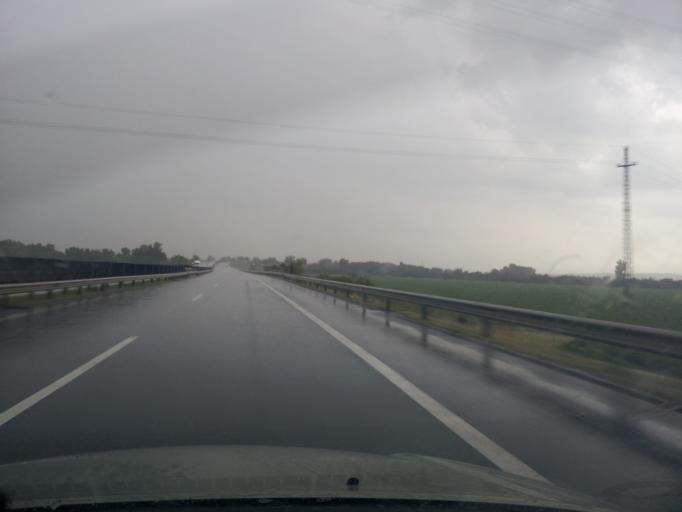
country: HU
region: Borsod-Abauj-Zemplen
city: Felsozsolca
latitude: 48.0950
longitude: 20.8480
